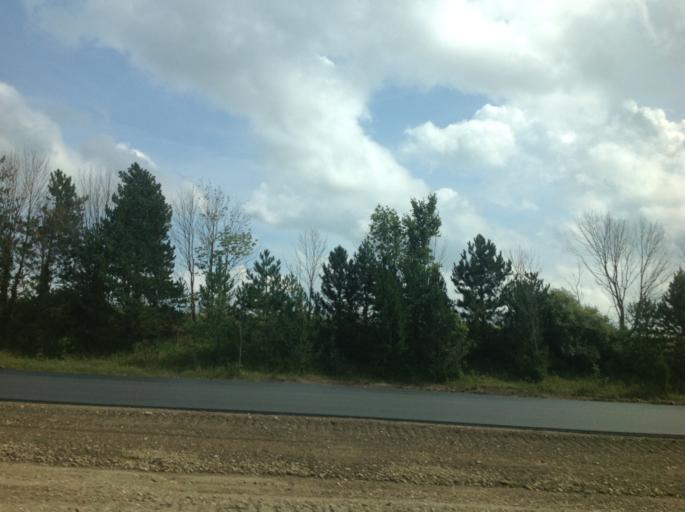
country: US
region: Ohio
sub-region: Delaware County
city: Ashley
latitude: 40.3617
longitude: -82.8470
